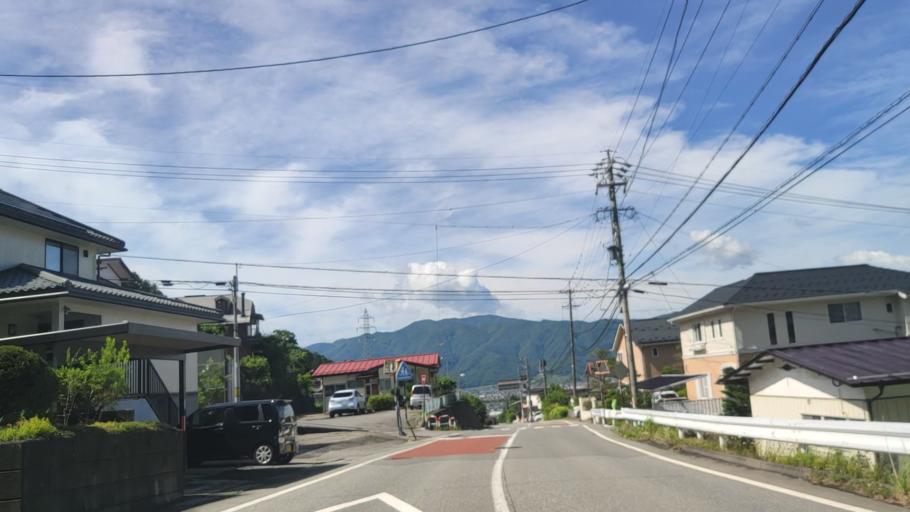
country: JP
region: Nagano
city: Suwa
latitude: 36.0470
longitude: 138.1281
